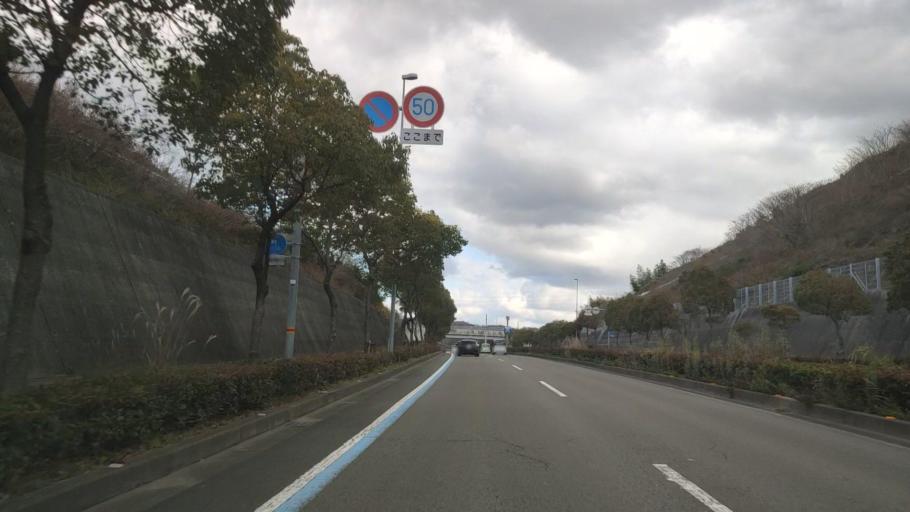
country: JP
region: Ehime
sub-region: Shikoku-chuo Shi
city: Matsuyama
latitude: 33.8895
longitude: 132.7565
